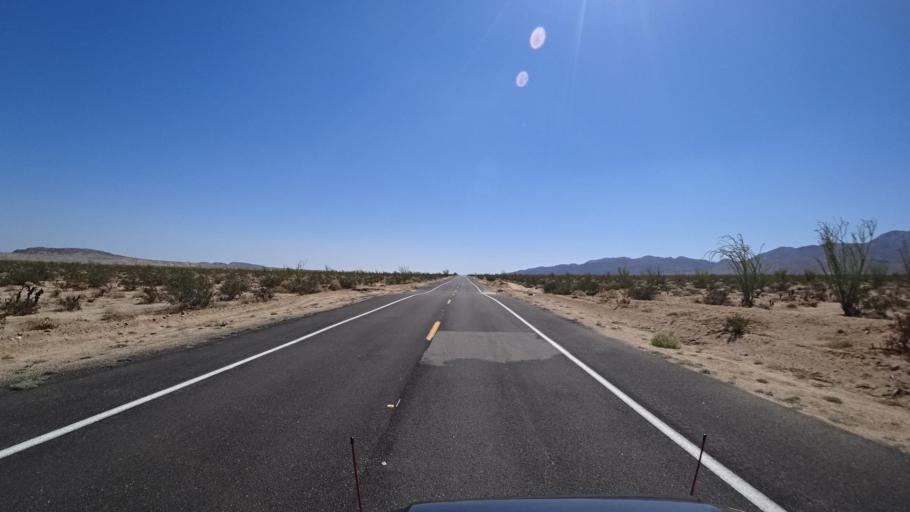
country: US
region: California
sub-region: San Diego County
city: Borrego Springs
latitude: 33.1742
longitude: -116.2705
